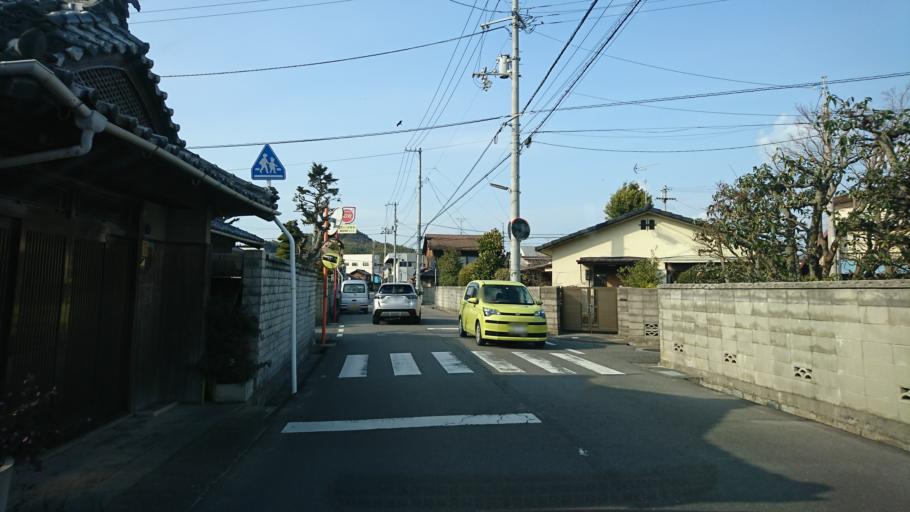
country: JP
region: Ehime
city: Saijo
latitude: 34.0206
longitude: 133.0404
